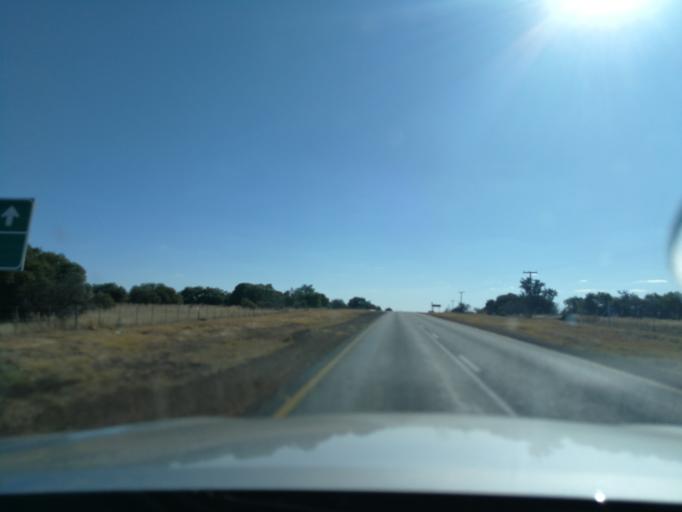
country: ZA
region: North-West
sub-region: Ngaka Modiri Molema District Municipality
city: Zeerust
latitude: -25.7635
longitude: 25.9771
